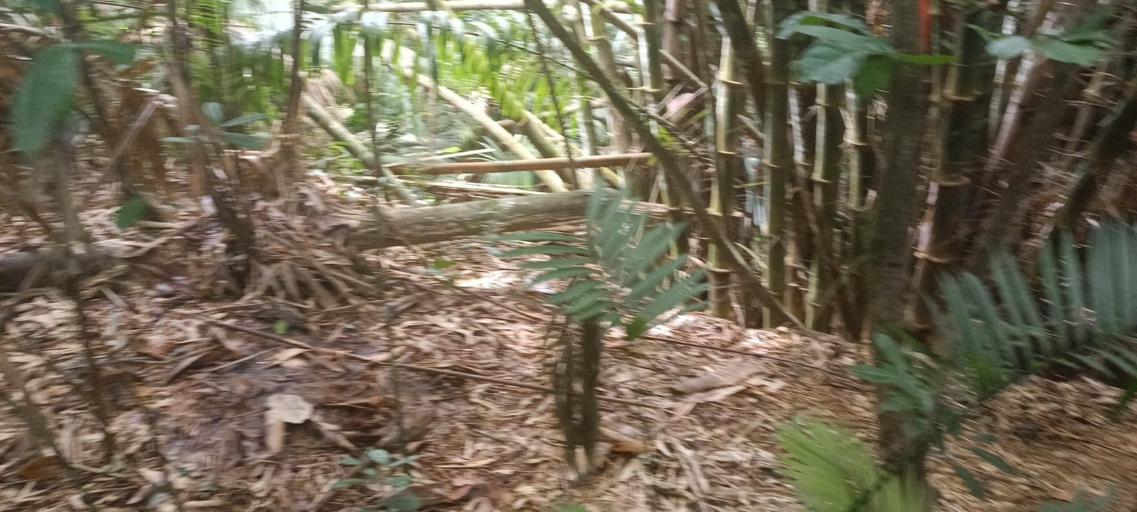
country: MY
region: Penang
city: Bukit Mertajam
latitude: 5.3722
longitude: 100.4992
